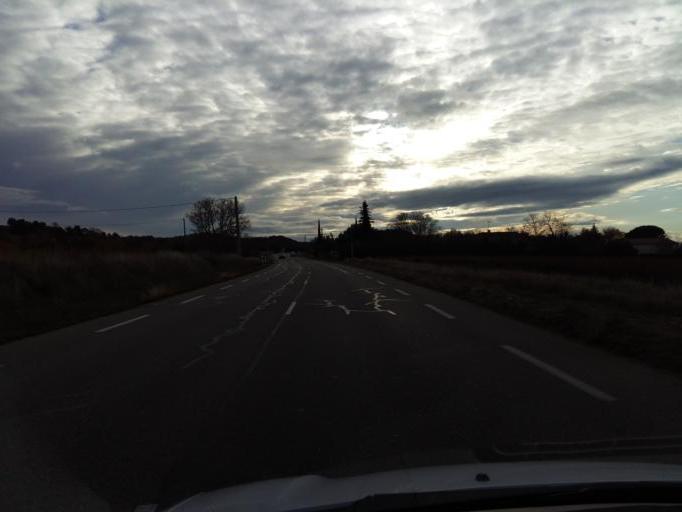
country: FR
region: Provence-Alpes-Cote d'Azur
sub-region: Departement du Vaucluse
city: Valreas
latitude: 44.3643
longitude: 4.9748
